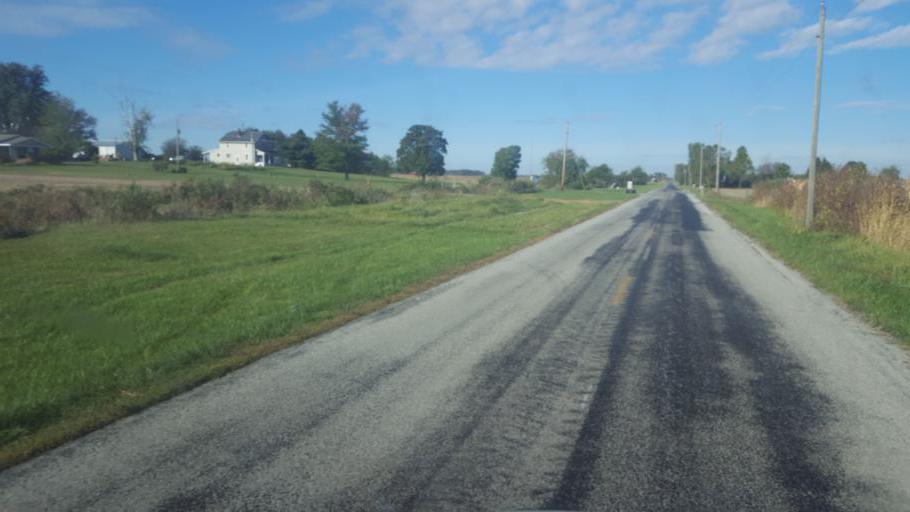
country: US
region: Ohio
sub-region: Crawford County
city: Bucyrus
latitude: 40.6886
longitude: -83.0257
